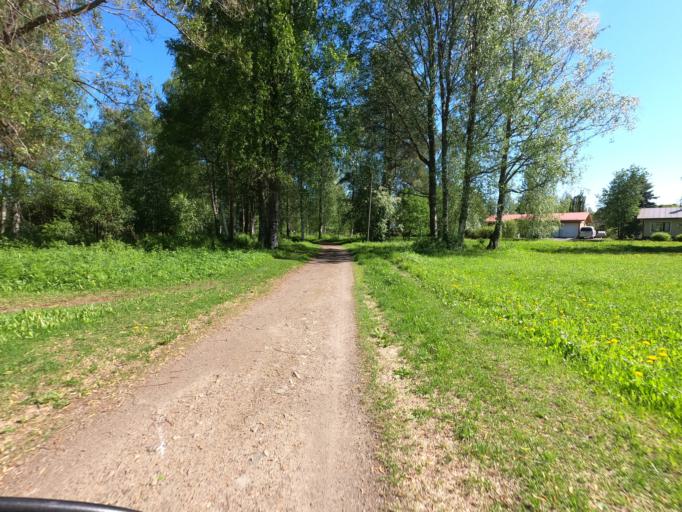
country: FI
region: North Karelia
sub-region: Joensuu
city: Joensuu
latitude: 62.6065
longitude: 29.8081
